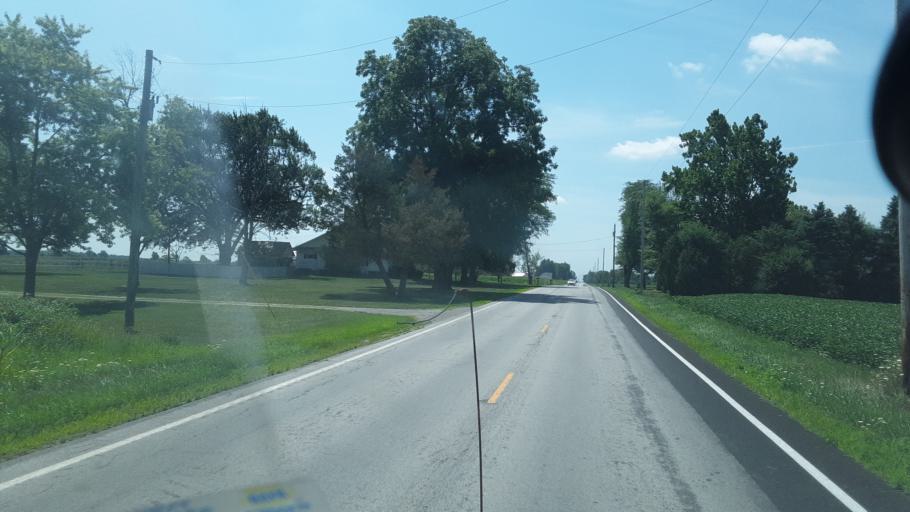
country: US
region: Ohio
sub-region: Hancock County
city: Arlington
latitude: 40.9679
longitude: -83.5746
